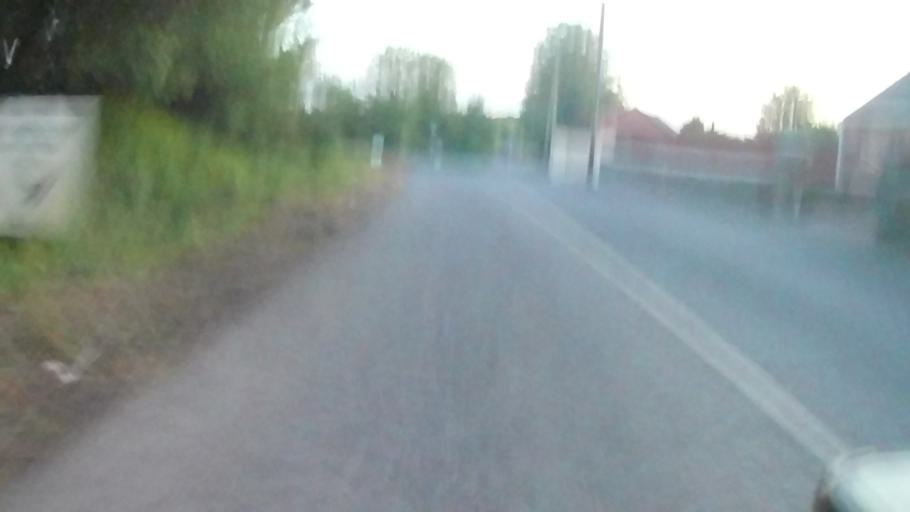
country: IE
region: Munster
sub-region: County Cork
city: Carrigtwohill
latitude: 51.9581
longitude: -8.3035
